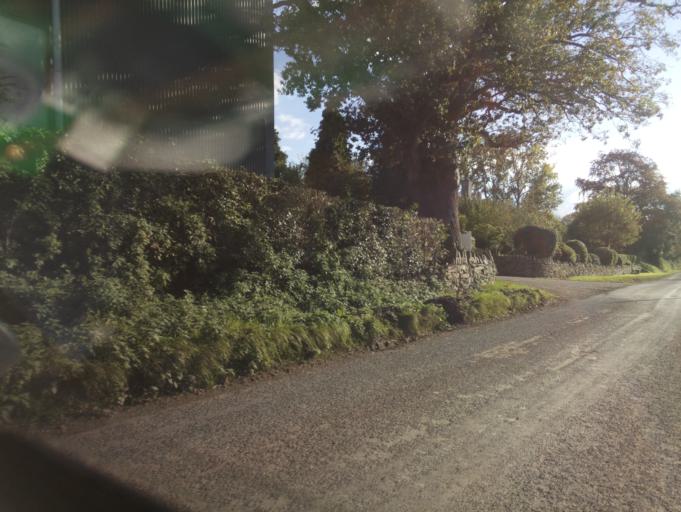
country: GB
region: England
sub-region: Herefordshire
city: Clifford
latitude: 52.1026
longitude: -3.1051
